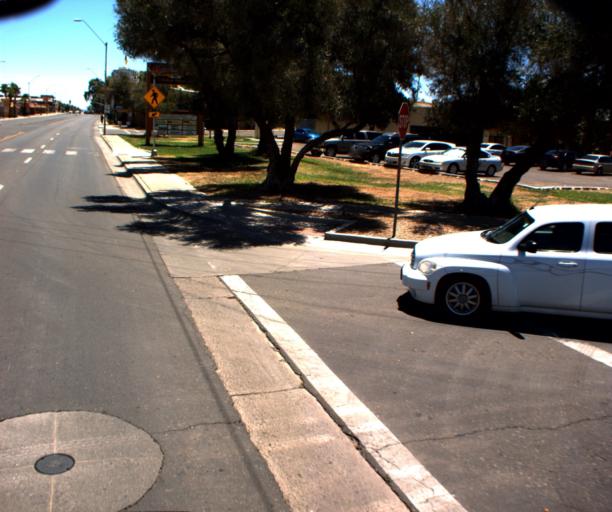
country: US
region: Arizona
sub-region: Pinal County
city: Casa Grande
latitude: 32.8795
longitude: -111.7544
